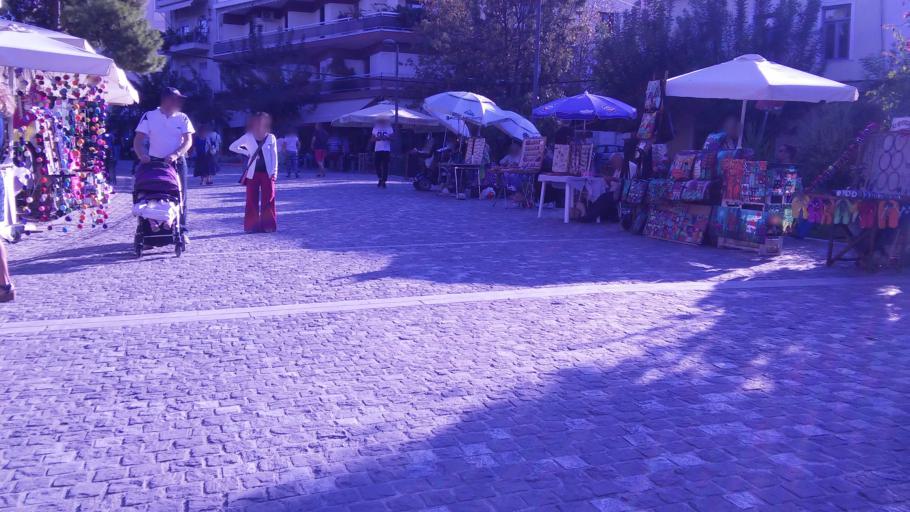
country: GR
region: Attica
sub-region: Nomarchia Athinas
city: Athens
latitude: 37.9759
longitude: 23.7196
